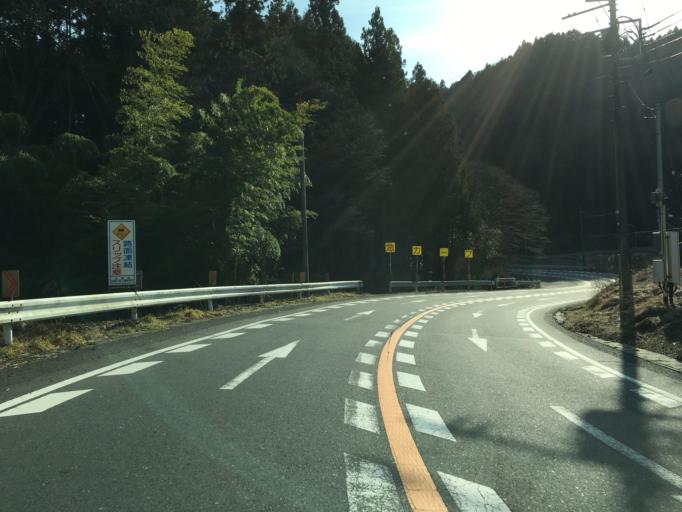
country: JP
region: Ibaraki
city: Daigo
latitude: 36.7301
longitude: 140.5120
